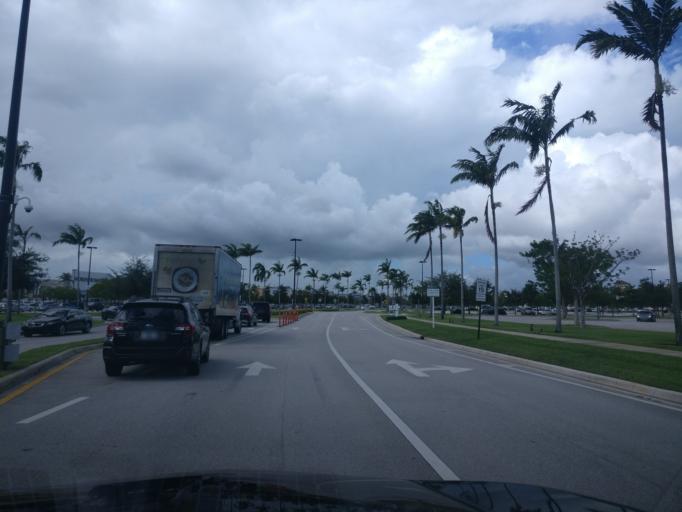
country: US
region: Florida
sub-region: Palm Beach County
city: Schall Circle
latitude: 26.7218
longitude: -80.0881
